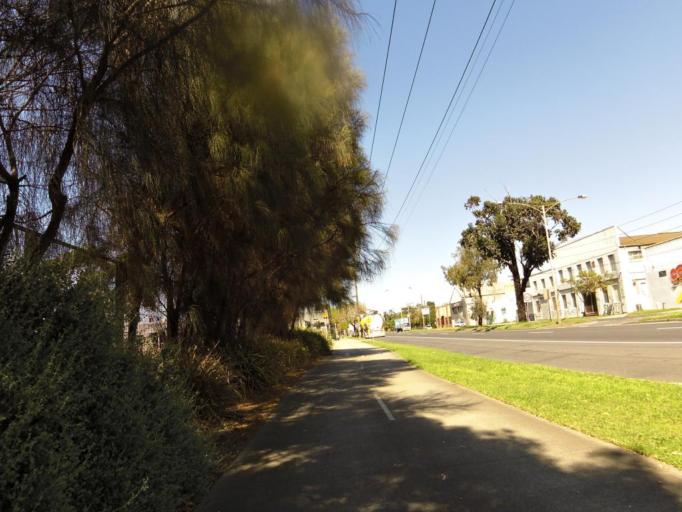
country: AU
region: Victoria
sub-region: Maribyrnong
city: Yarraville
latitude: -37.8107
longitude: 144.9019
